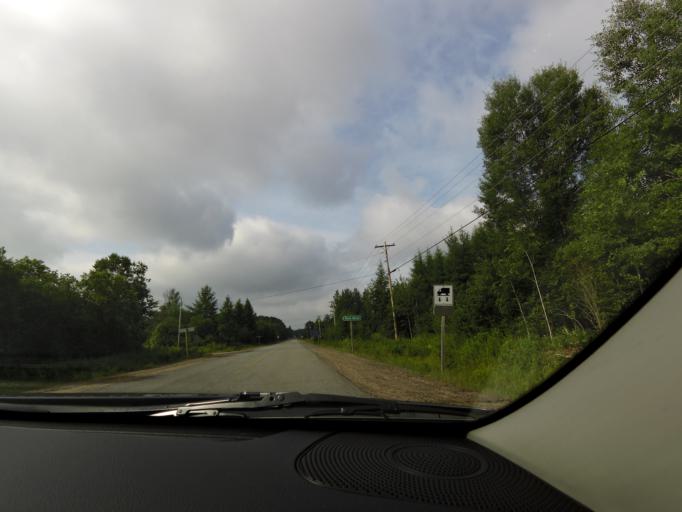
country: CA
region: Ontario
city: Huntsville
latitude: 45.5674
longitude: -79.2256
